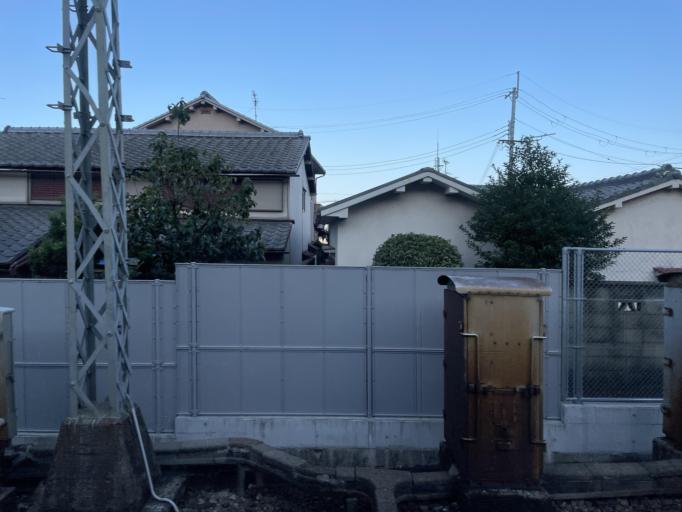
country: JP
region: Osaka
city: Daitocho
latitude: 34.6678
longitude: 135.6476
